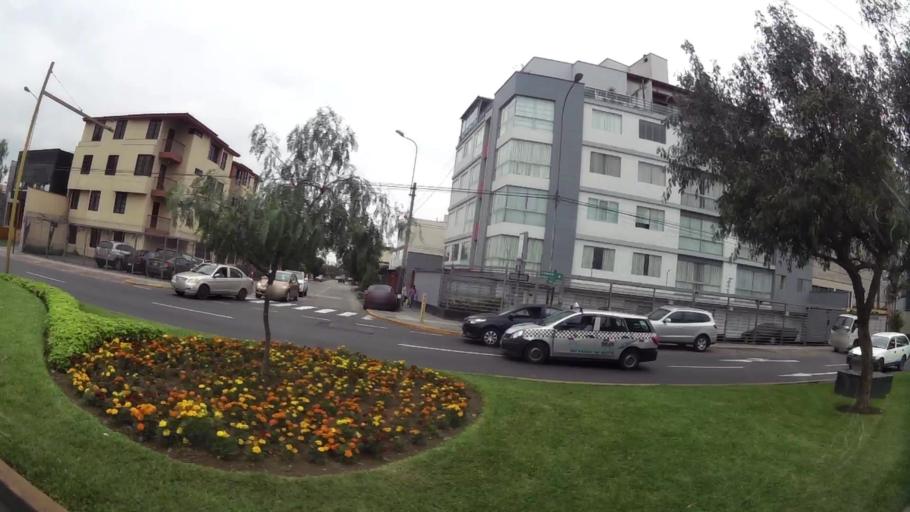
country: PE
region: Lima
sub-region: Lima
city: Surco
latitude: -12.1180
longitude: -76.9893
